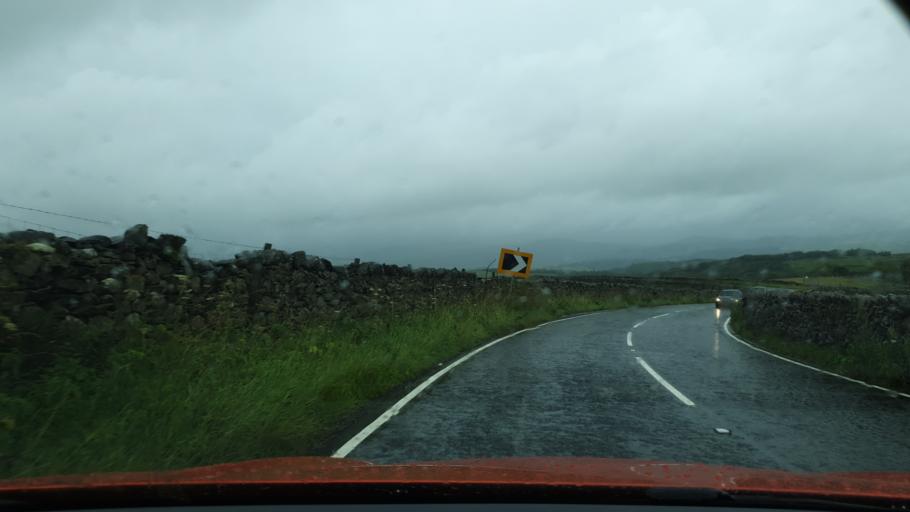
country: GB
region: England
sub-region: Cumbria
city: Ulverston
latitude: 54.2553
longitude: -3.1415
